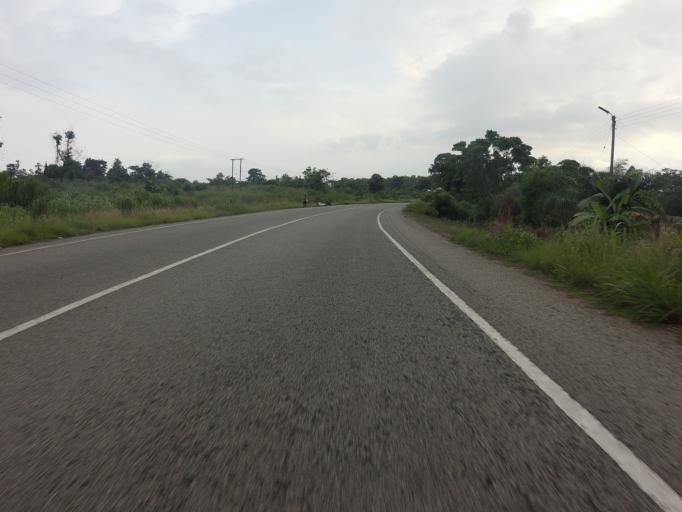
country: GH
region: Volta
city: Ho
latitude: 6.7844
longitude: 0.4495
